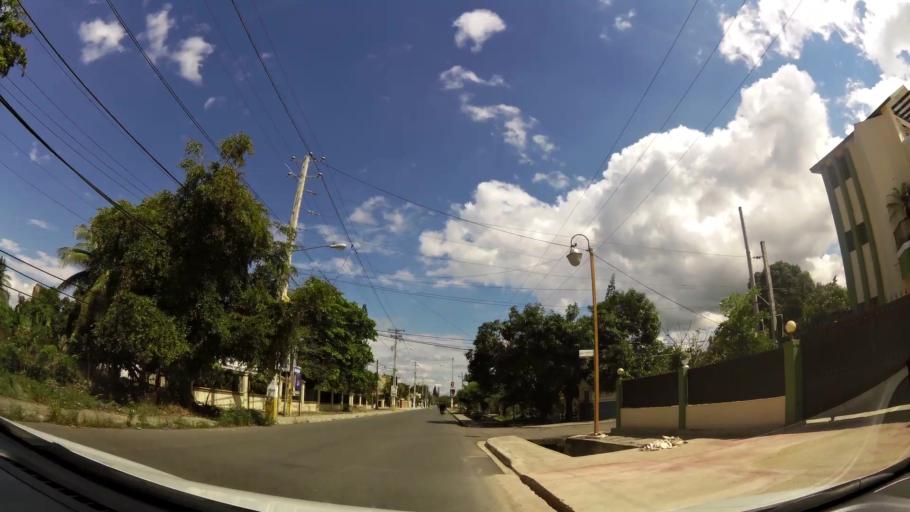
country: DO
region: Santiago
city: Licey al Medio
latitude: 19.3844
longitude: -70.6251
